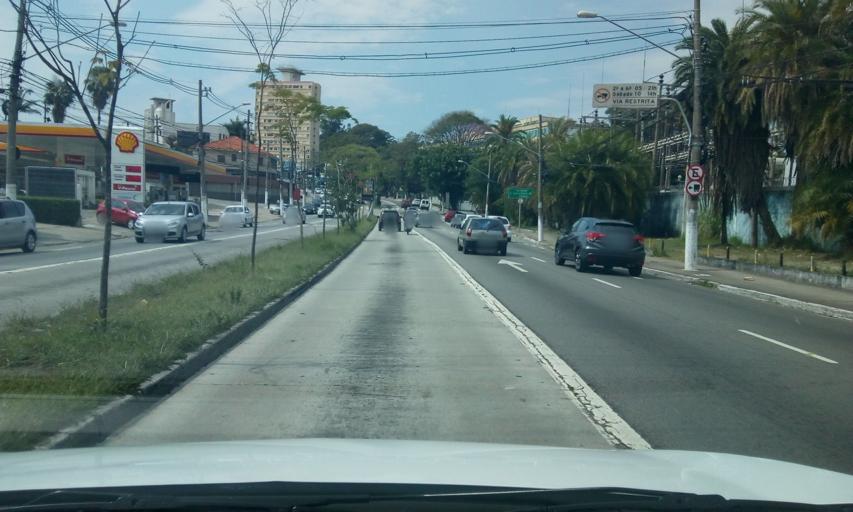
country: BR
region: Sao Paulo
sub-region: Sao Paulo
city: Sao Paulo
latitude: -23.5791
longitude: -46.7100
